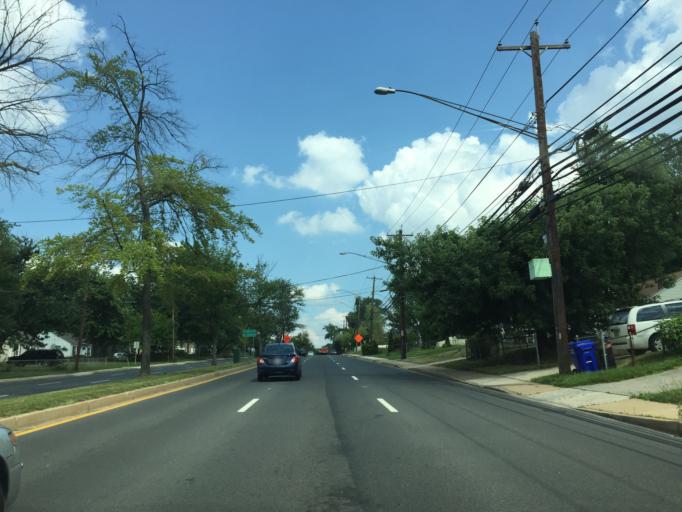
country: US
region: Maryland
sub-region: Montgomery County
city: Glenmont
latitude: 39.0588
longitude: -77.0574
